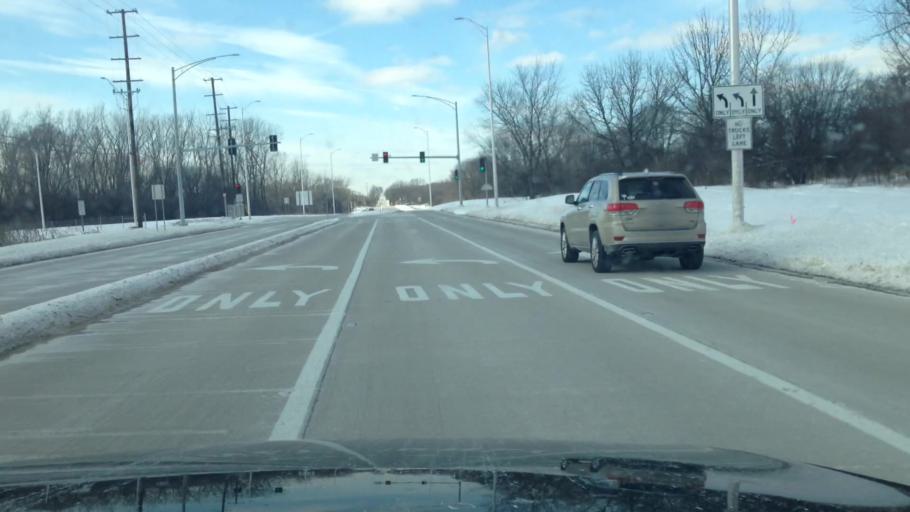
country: US
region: Illinois
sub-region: Cook County
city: Hoffman Estates
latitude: 42.0670
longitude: -88.0852
